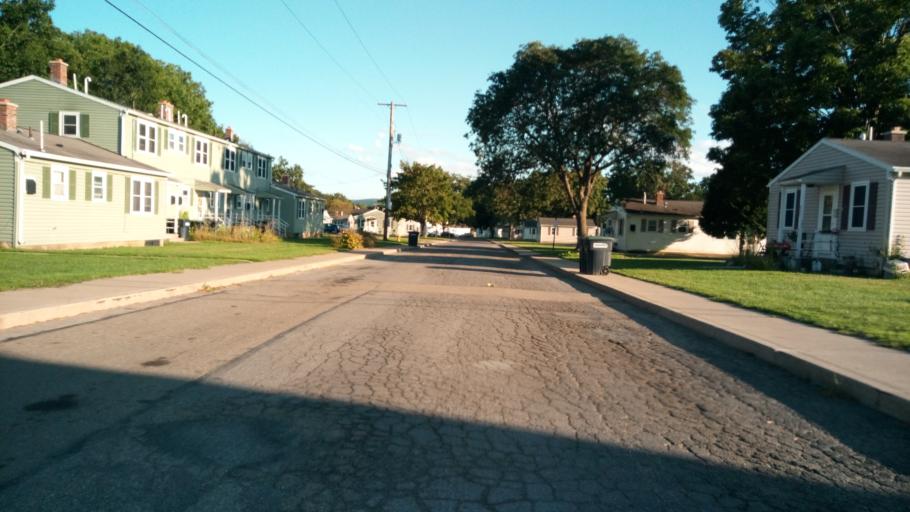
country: US
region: New York
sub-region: Chemung County
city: West Elmira
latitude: 42.0996
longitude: -76.8326
